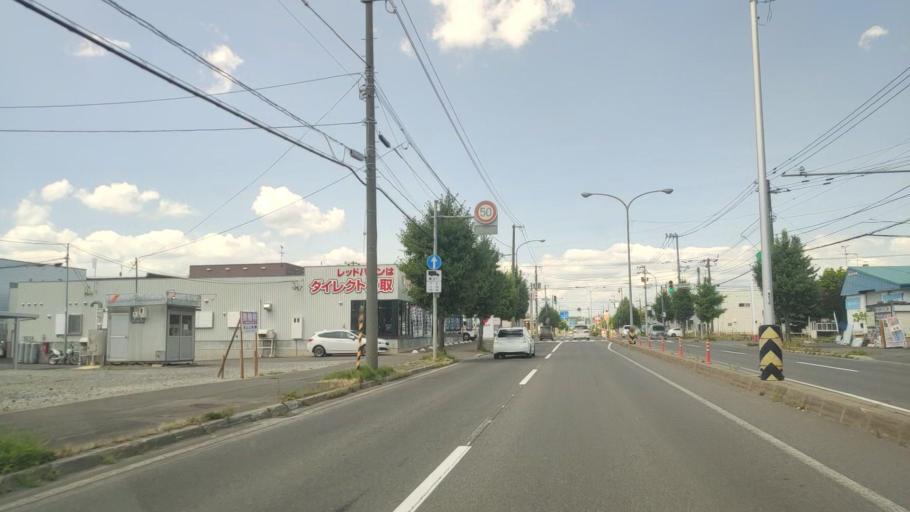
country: JP
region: Hokkaido
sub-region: Asahikawa-shi
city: Asahikawa
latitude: 43.8009
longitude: 142.3922
